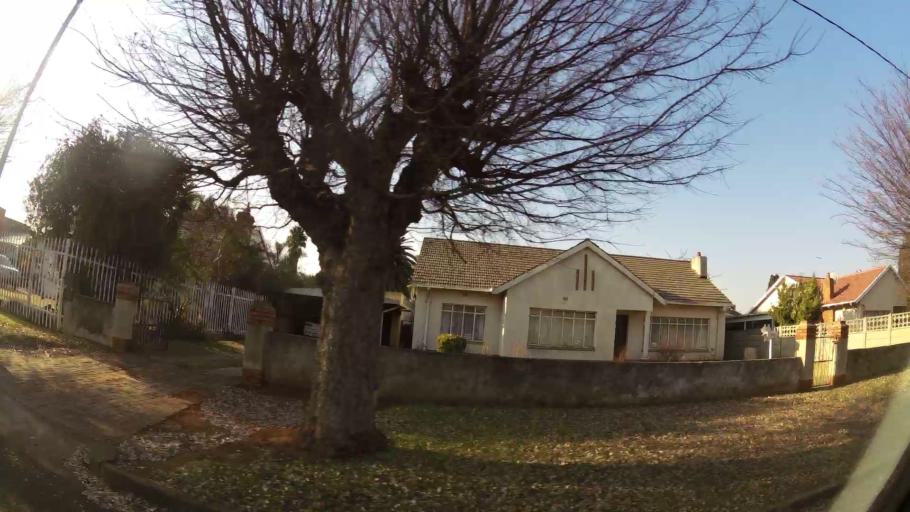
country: ZA
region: Gauteng
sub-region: Ekurhuleni Metropolitan Municipality
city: Springs
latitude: -26.2582
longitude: 28.3890
